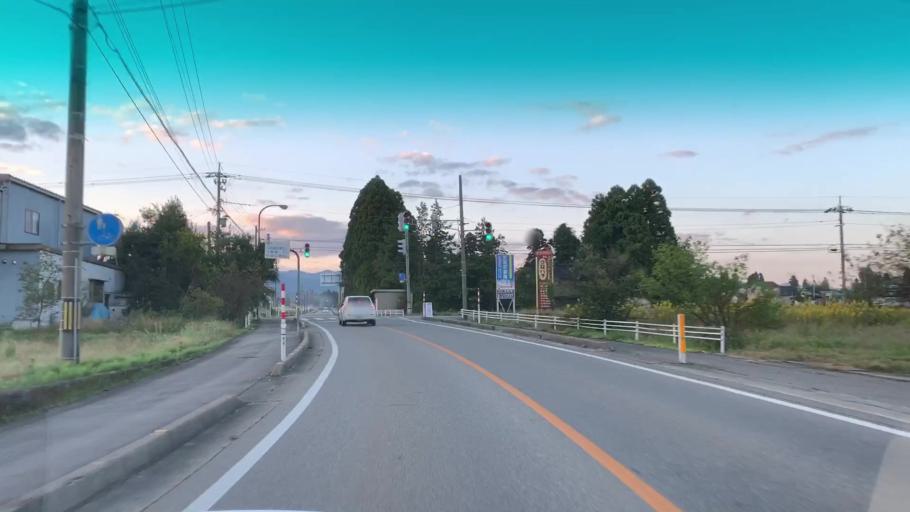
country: JP
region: Toyama
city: Kamiichi
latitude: 36.6624
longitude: 137.3271
